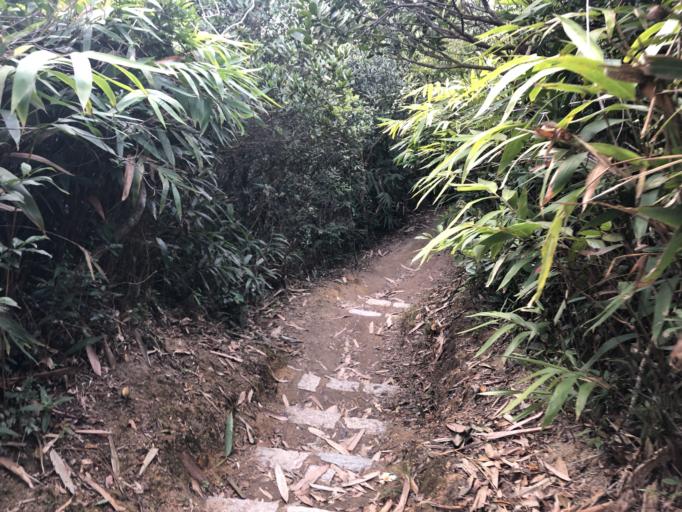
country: HK
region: Wanchai
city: Wan Chai
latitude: 22.2687
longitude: 114.2098
